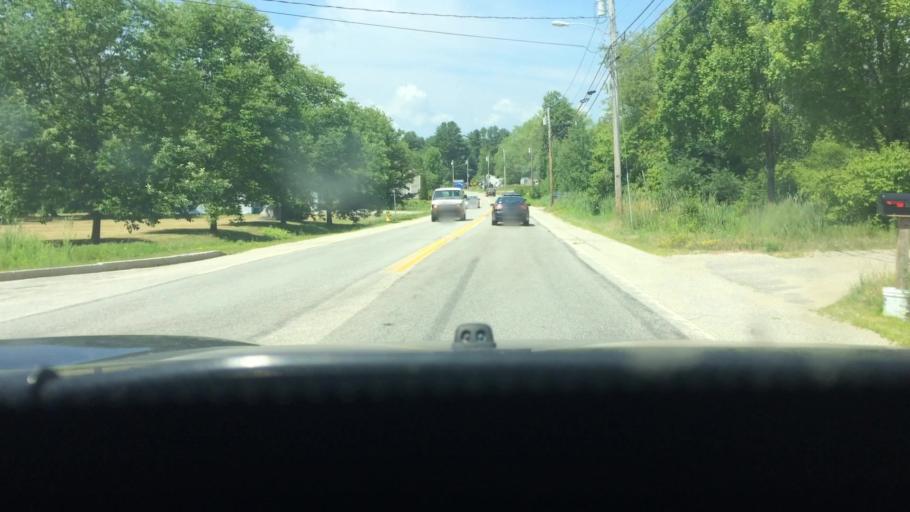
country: US
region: Maine
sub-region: Androscoggin County
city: Mechanic Falls
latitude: 44.1147
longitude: -70.4009
